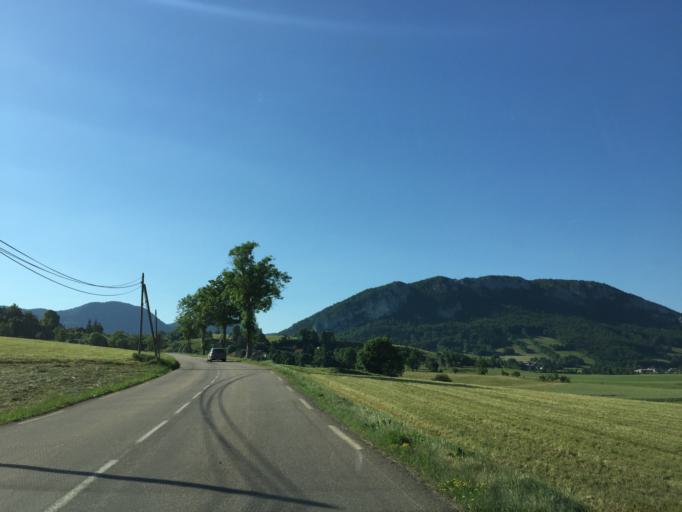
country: FR
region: Rhone-Alpes
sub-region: Departement de la Drome
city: Saint-Laurent-en-Royans
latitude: 44.9733
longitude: 5.4032
